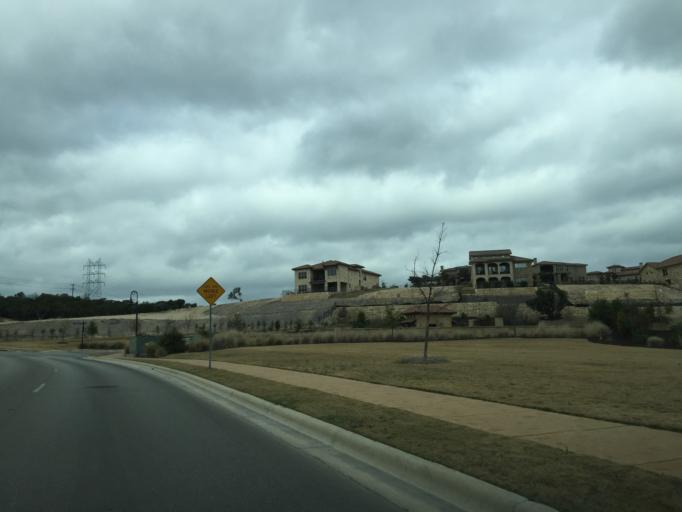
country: US
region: Texas
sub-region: Travis County
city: The Hills
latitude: 30.3499
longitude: -98.0147
